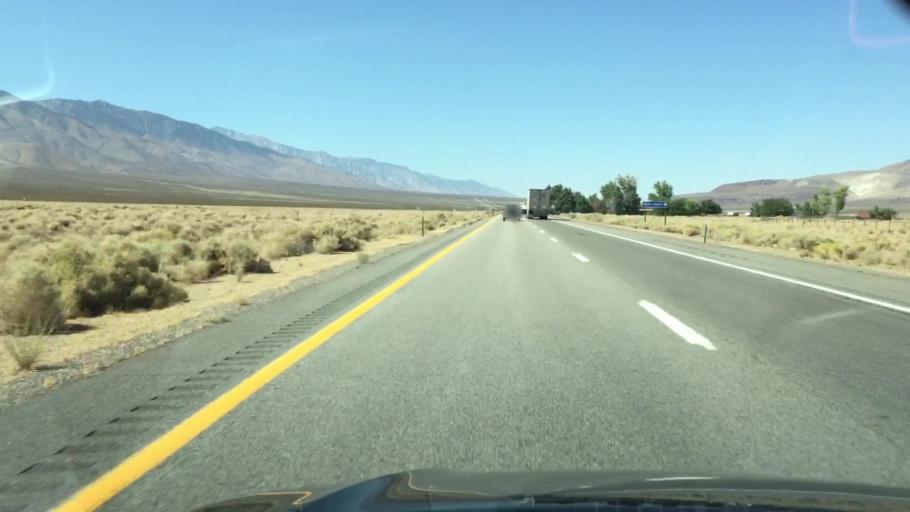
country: US
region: California
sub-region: Kern County
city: Inyokern
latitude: 36.0418
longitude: -117.9460
